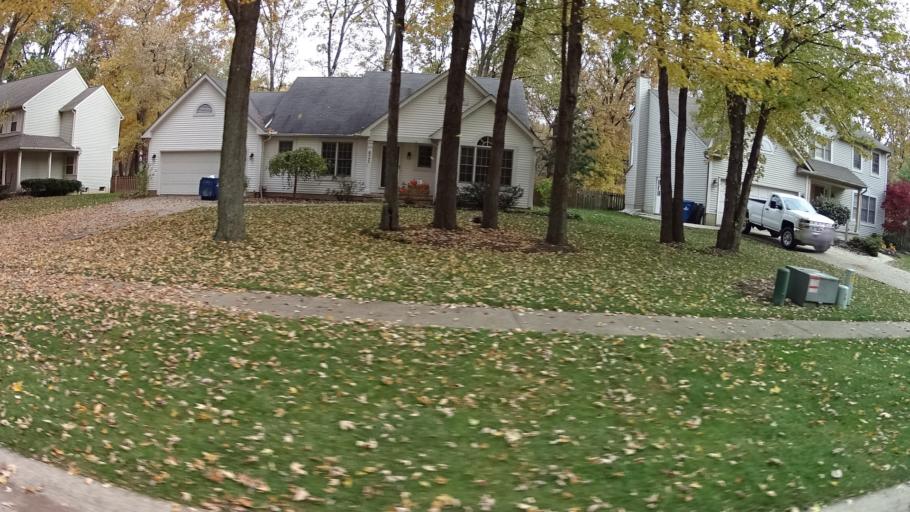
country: US
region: Ohio
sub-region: Lorain County
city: Sheffield Lake
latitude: 41.4842
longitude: -82.0933
